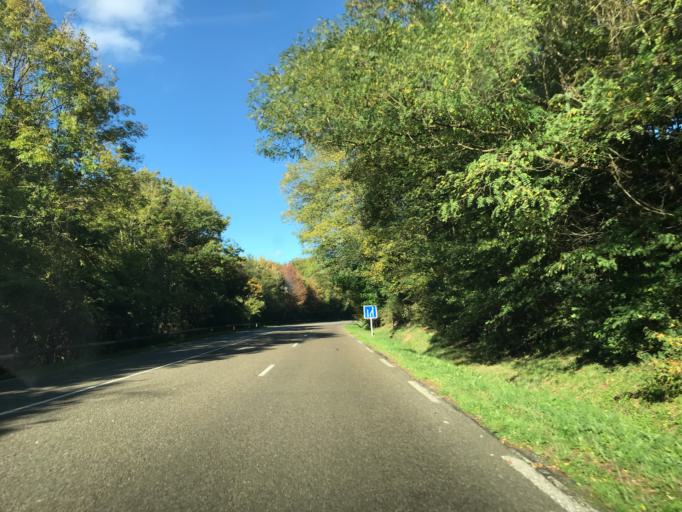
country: FR
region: Haute-Normandie
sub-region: Departement de l'Eure
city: Saint-Aubin-sur-Gaillon
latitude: 49.1174
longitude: 1.3032
